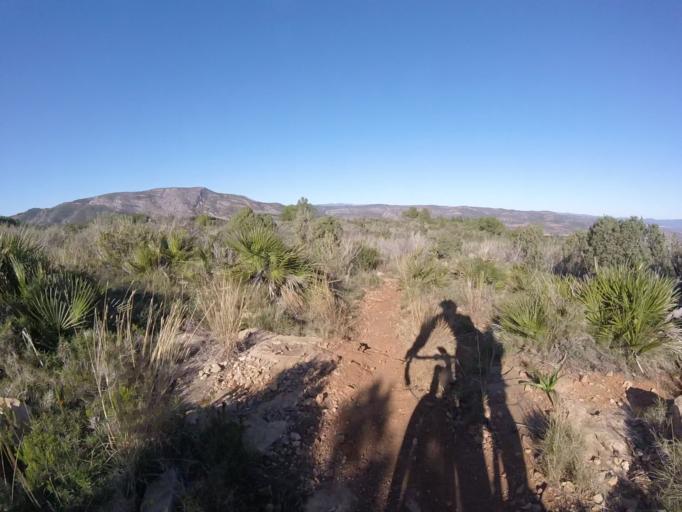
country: ES
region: Valencia
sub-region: Provincia de Castello
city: Orpesa/Oropesa del Mar
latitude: 40.1117
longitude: 0.1170
